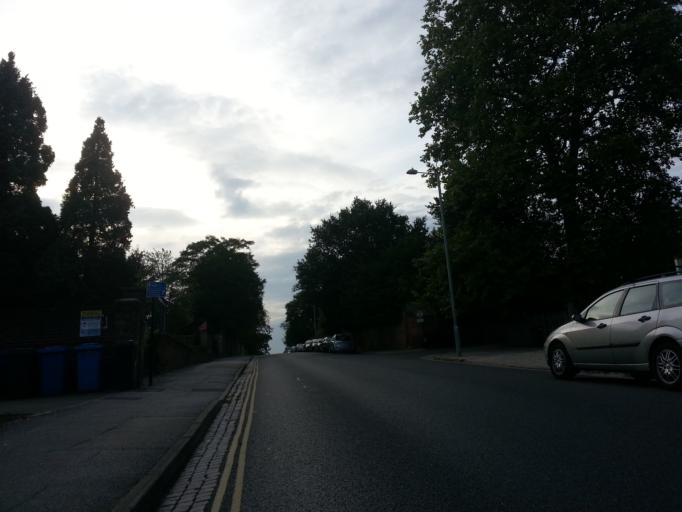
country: GB
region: England
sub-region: Suffolk
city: Ipswich
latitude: 52.0607
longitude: 1.1548
